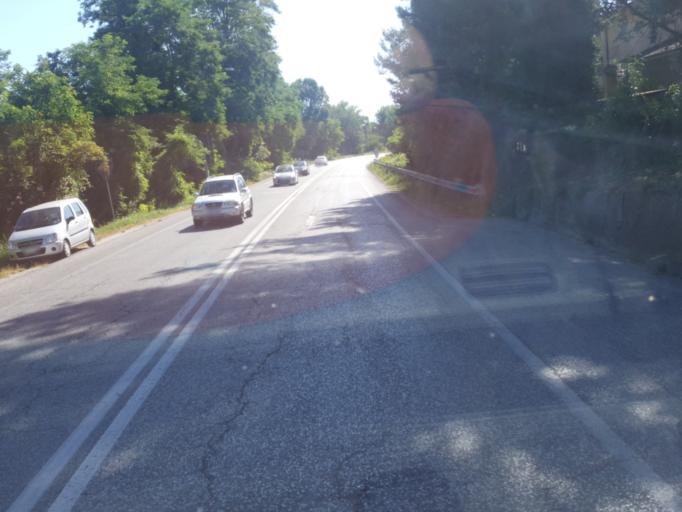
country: IT
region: The Marches
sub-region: Provincia di Pesaro e Urbino
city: Montelabbate
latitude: 43.8504
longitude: 12.7864
